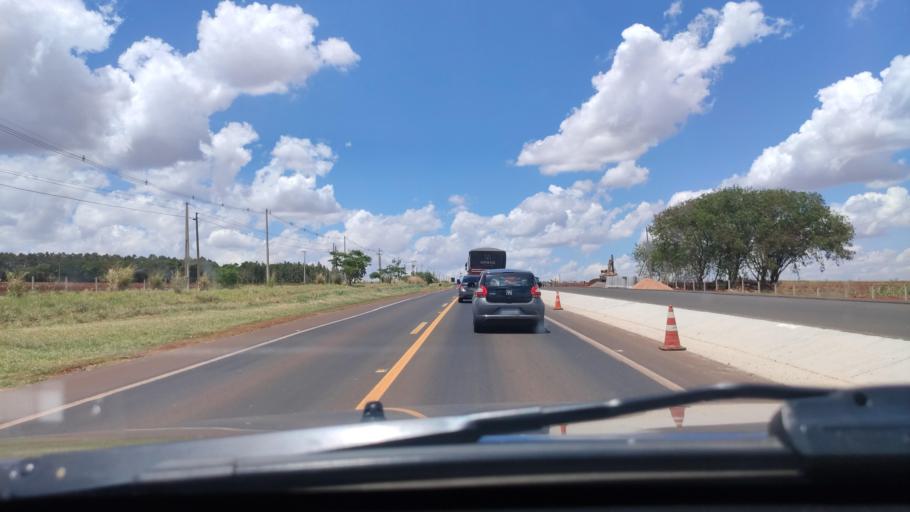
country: BR
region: Sao Paulo
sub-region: Jau
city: Jau
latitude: -22.2434
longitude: -48.5412
